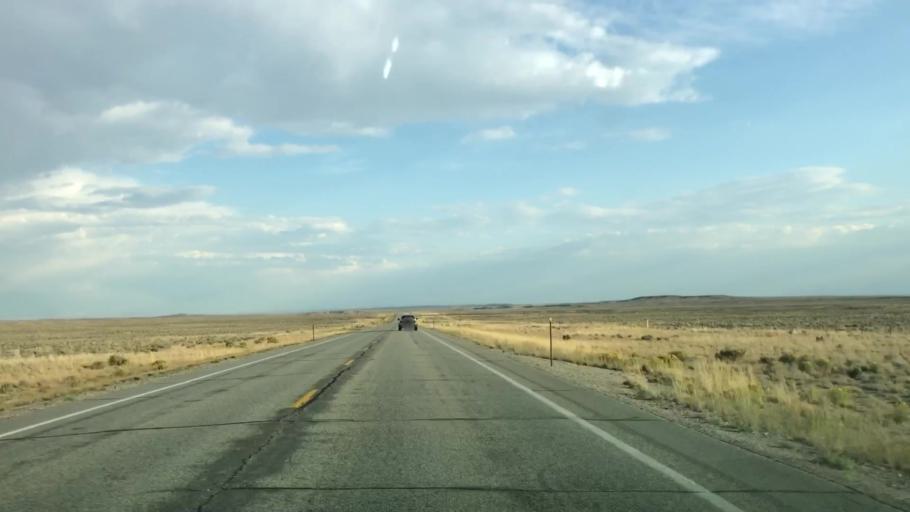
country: US
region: Wyoming
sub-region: Sublette County
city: Pinedale
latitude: 42.3870
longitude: -109.5382
